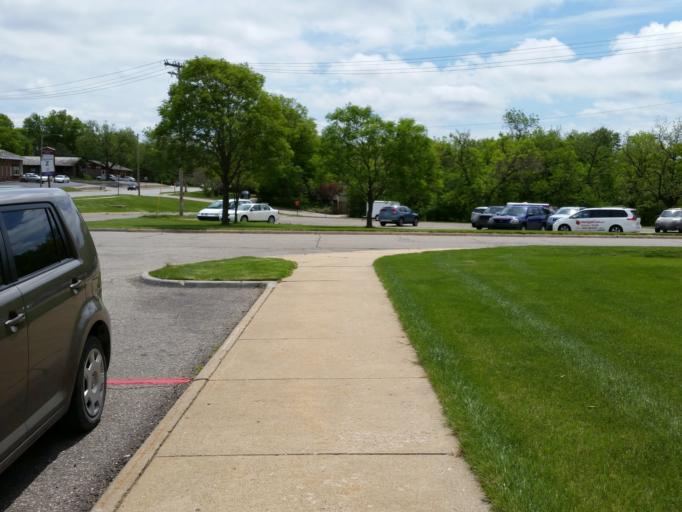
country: US
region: Kansas
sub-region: Riley County
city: Manhattan
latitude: 39.1885
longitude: -96.5995
